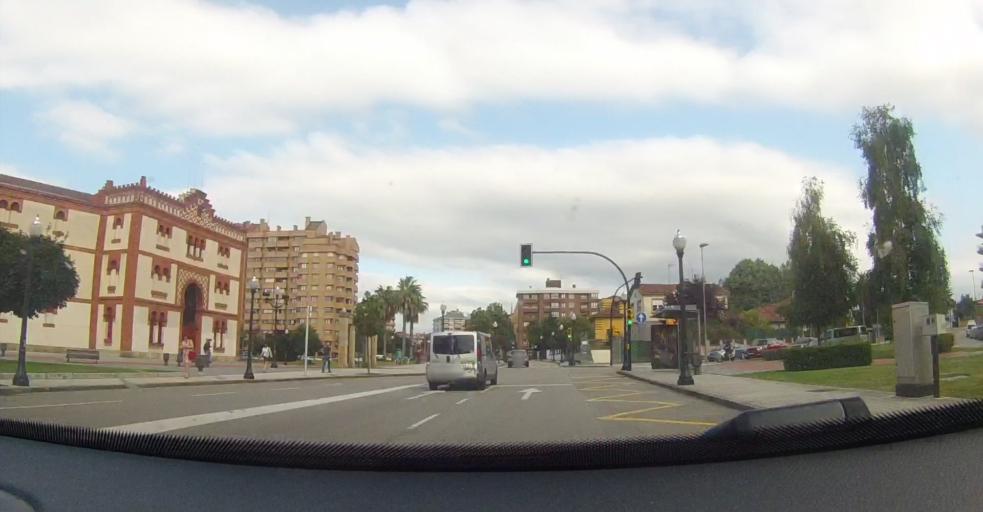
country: ES
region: Asturias
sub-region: Province of Asturias
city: Gijon
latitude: 43.5351
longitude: -5.6464
